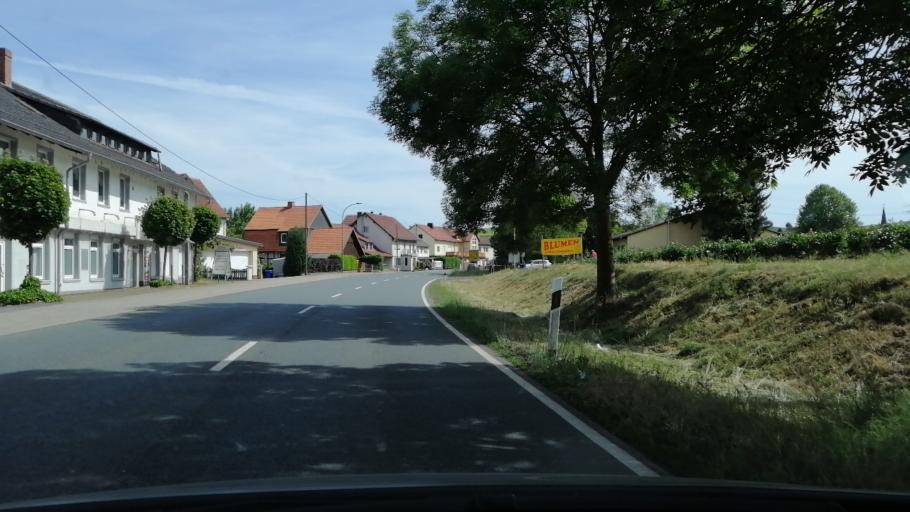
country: DE
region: Hesse
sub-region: Regierungsbezirk Kassel
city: Bad Wildungen
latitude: 51.1587
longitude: 9.1227
